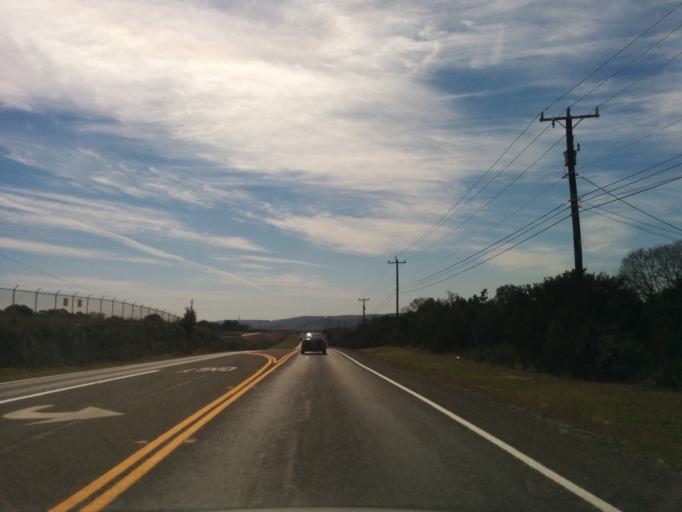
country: US
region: Texas
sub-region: Bexar County
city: Scenic Oaks
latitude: 29.6952
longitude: -98.6316
